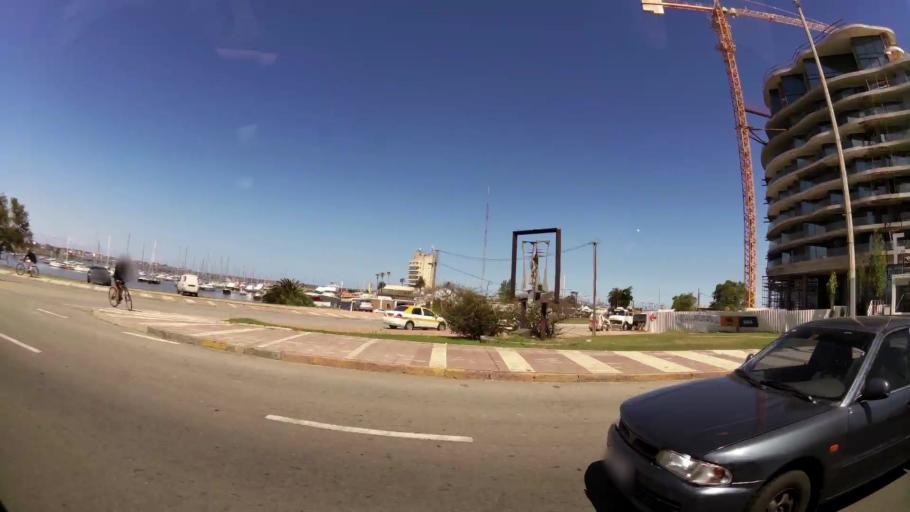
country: UY
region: Montevideo
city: Montevideo
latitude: -34.9092
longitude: -56.1336
